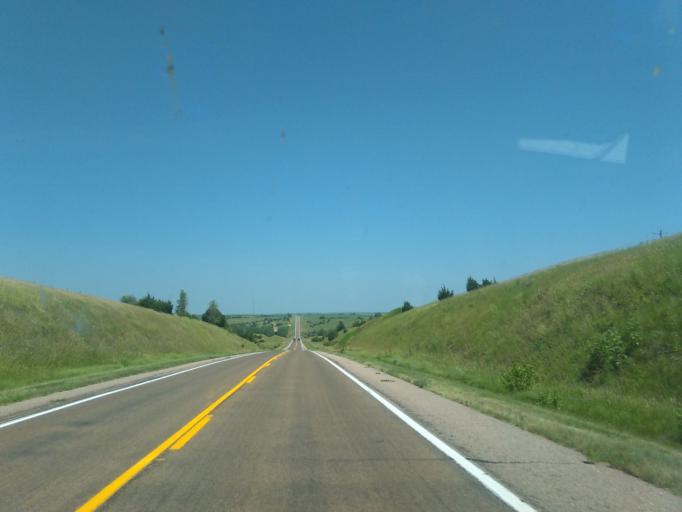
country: US
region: Nebraska
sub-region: Frontier County
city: Stockville
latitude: 40.6196
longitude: -100.6304
